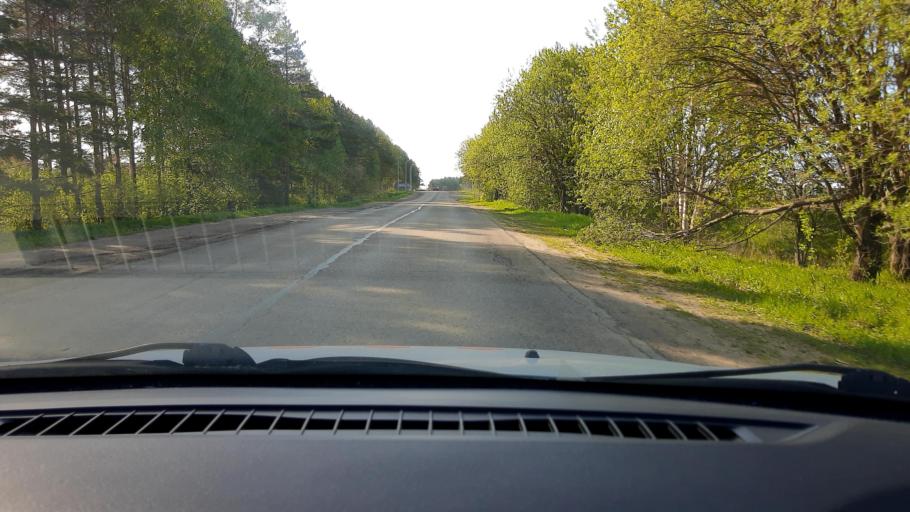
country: RU
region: Nizjnij Novgorod
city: Burevestnik
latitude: 56.1648
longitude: 43.7702
